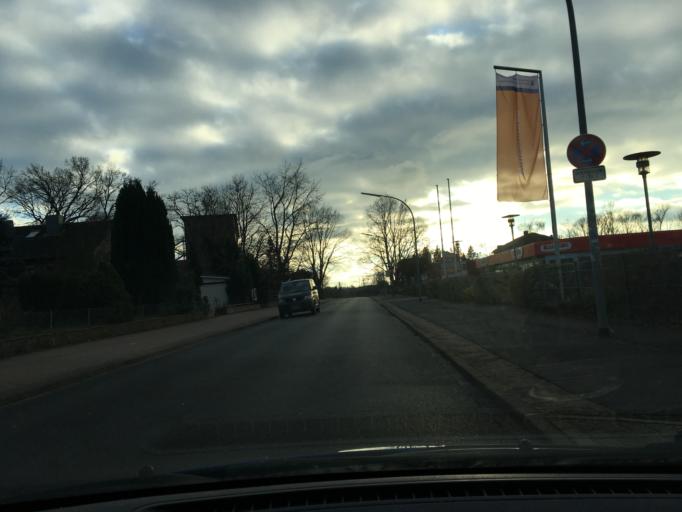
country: DE
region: Lower Saxony
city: Lueneburg
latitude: 53.2468
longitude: 10.4227
